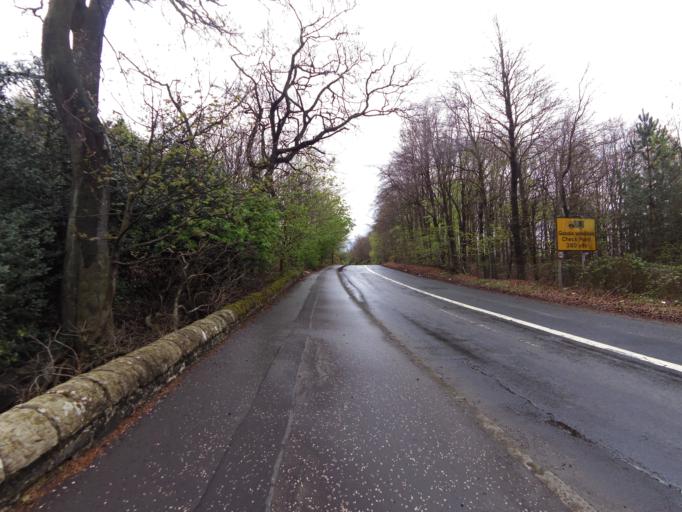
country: GB
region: Scotland
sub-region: Edinburgh
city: Ratho
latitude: 55.9707
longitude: -3.3255
